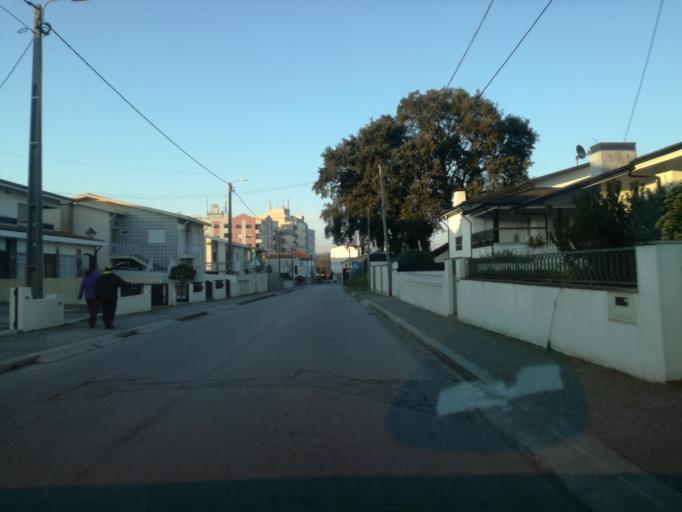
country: PT
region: Porto
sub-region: Maia
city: Milheiros
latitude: 41.2276
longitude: -8.5888
